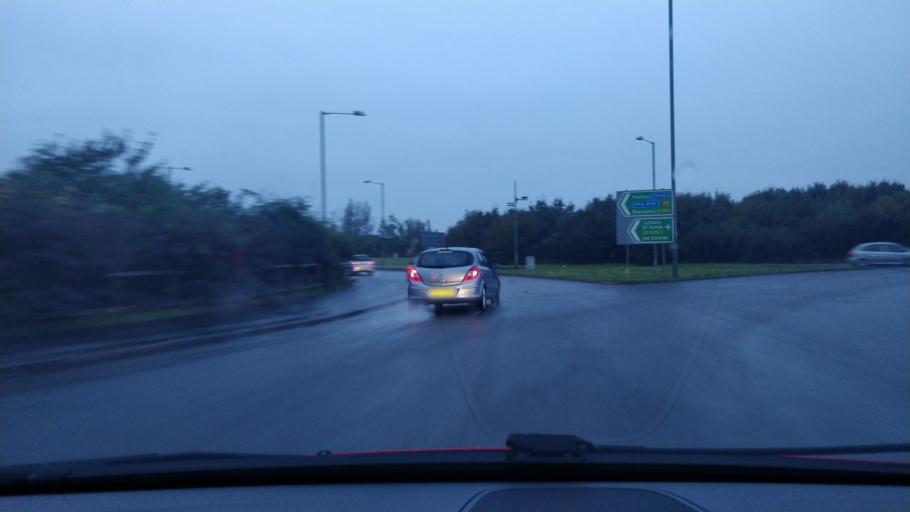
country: GB
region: England
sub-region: Lancashire
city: Poulton le Fylde
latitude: 53.7899
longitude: -2.9826
